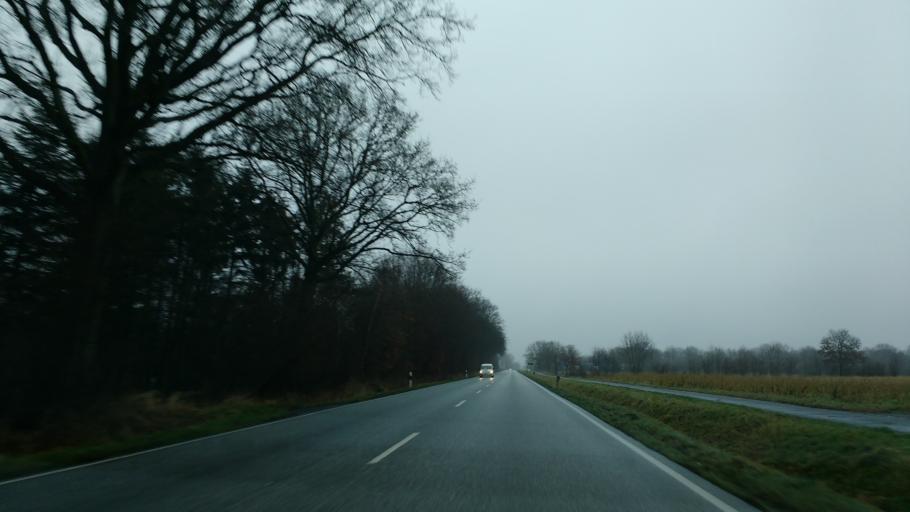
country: DE
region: Schleswig-Holstein
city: Brinjahe
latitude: 54.1911
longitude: 9.6417
